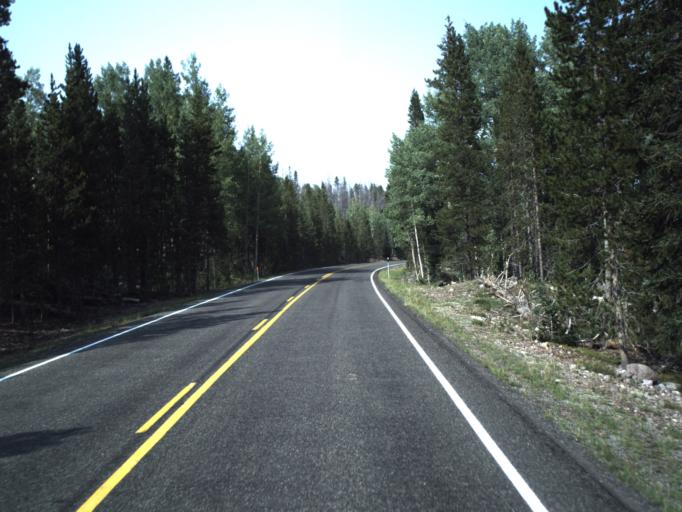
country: US
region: Utah
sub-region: Summit County
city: Oakley
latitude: 40.8044
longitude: -110.8794
